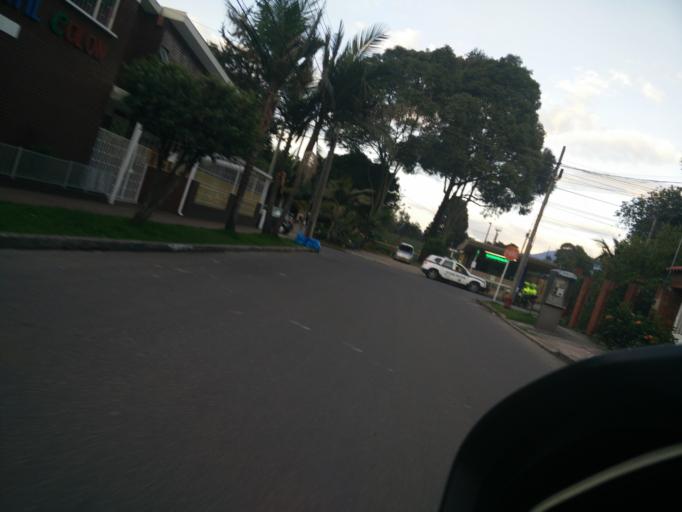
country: CO
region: Bogota D.C.
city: Bogota
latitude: 4.6460
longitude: -74.0911
